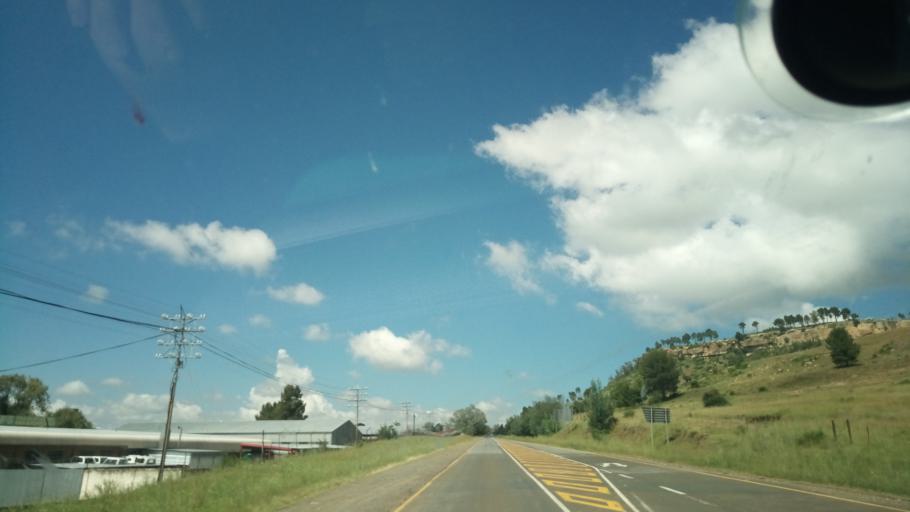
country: ZA
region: Orange Free State
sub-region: Thabo Mofutsanyana District Municipality
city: Ficksburg
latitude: -28.8545
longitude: 27.8790
